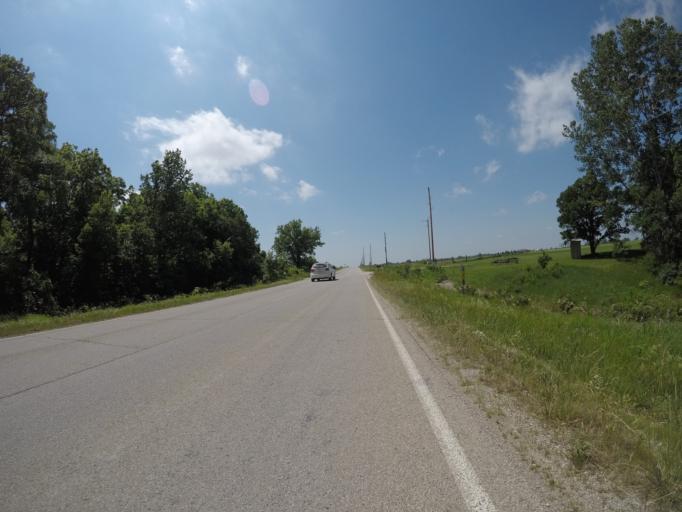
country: US
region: Kansas
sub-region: Pottawatomie County
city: Westmoreland
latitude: 39.3401
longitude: -96.4361
